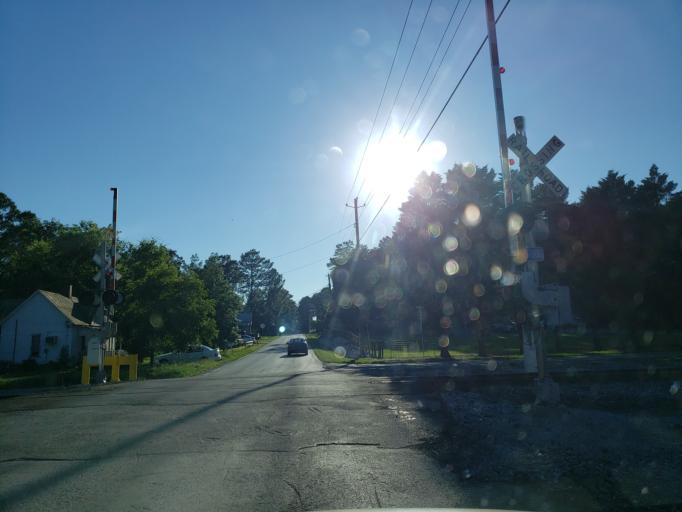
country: US
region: Georgia
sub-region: Polk County
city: Aragon
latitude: 34.0425
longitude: -85.0633
